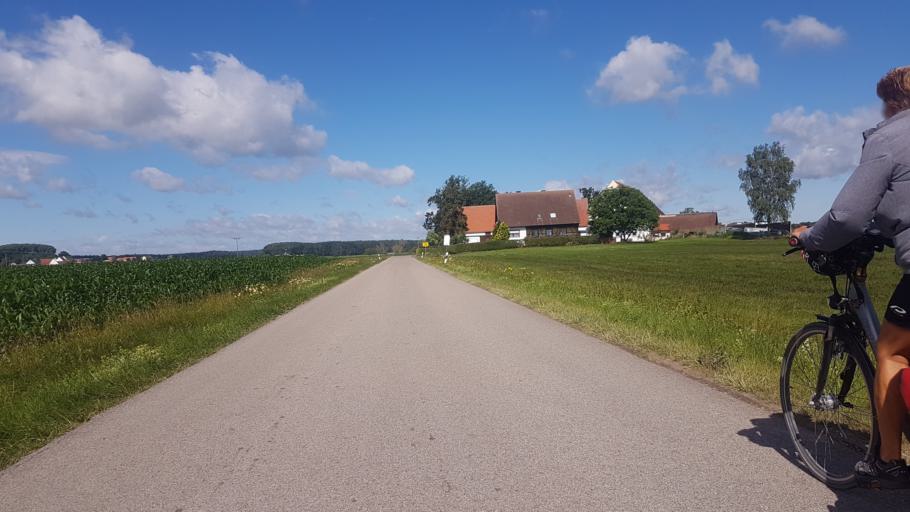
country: DE
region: Bavaria
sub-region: Regierungsbezirk Mittelfranken
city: Weidenbach
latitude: 49.1825
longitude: 10.6254
